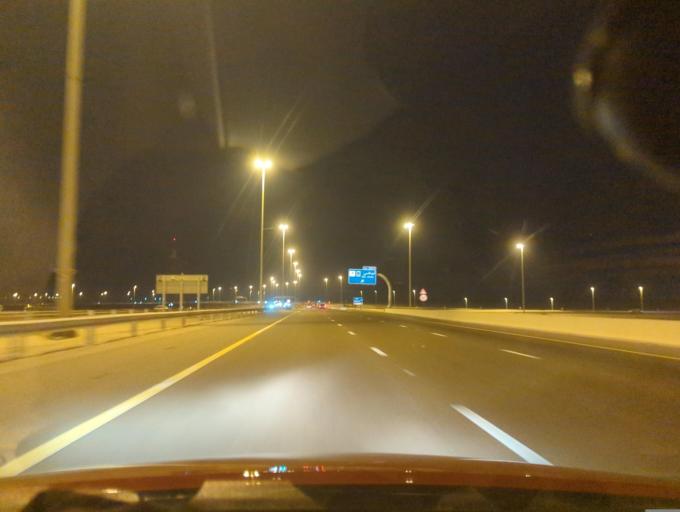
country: AE
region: Abu Dhabi
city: Abu Dhabi
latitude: 24.4203
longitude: 54.7634
